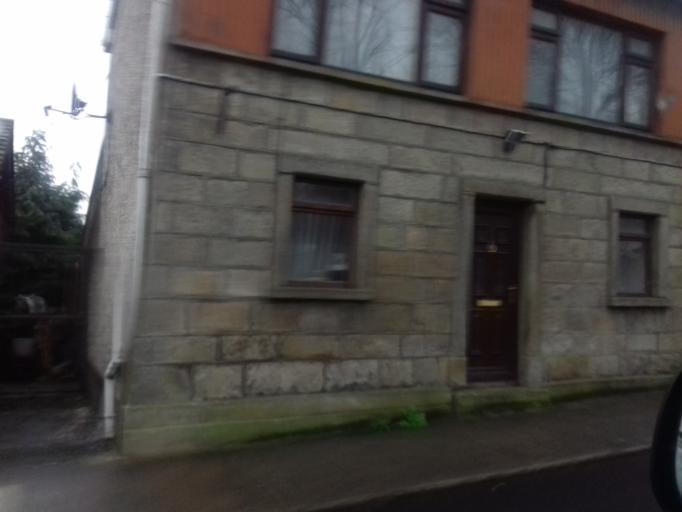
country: IE
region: Leinster
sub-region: Kilkenny
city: Graiguenamanagh
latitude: 52.5428
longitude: -6.9569
